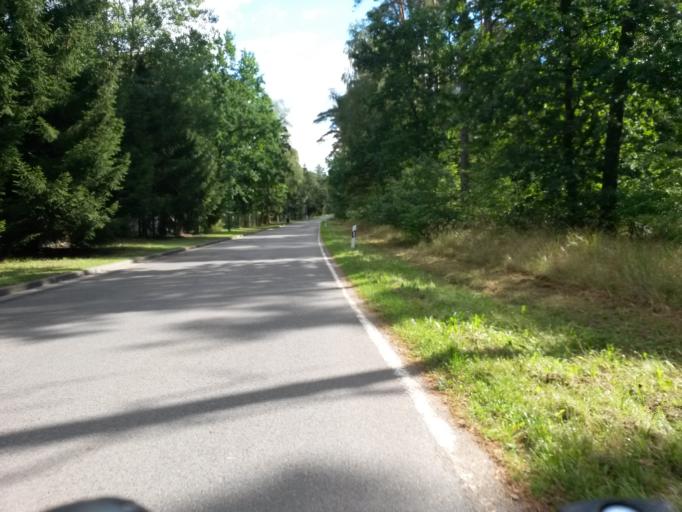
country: DE
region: Brandenburg
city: Templin
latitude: 53.2145
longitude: 13.5163
